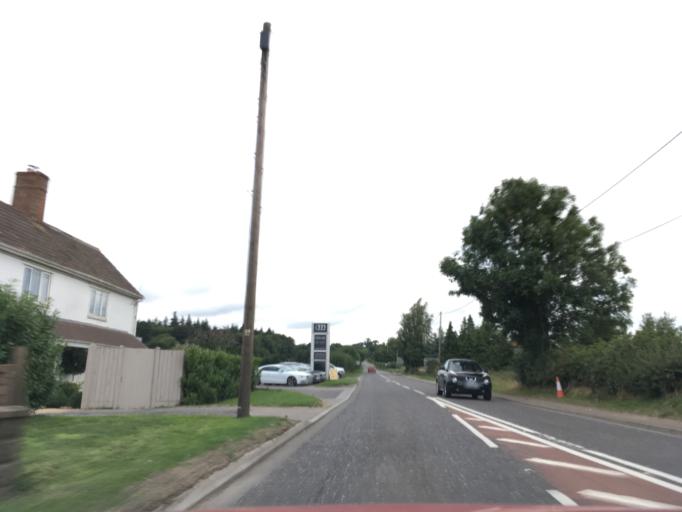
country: GB
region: England
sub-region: Wiltshire
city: Calne
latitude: 51.3966
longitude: -2.0452
